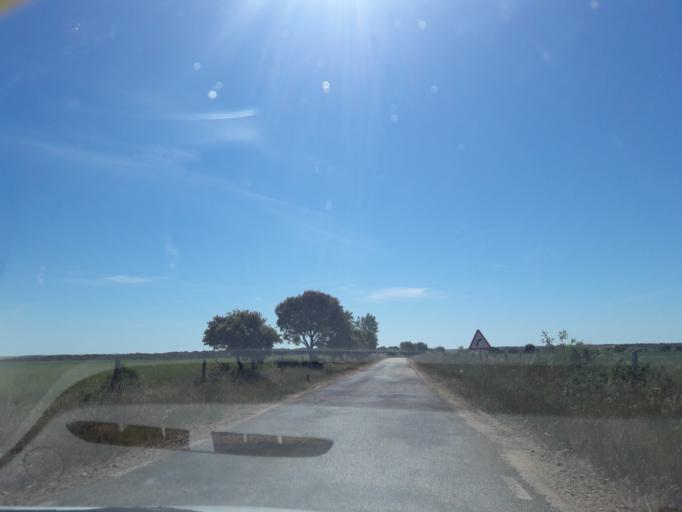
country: ES
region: Castille and Leon
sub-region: Provincia de Salamanca
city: Vega de Tirados
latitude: 41.0501
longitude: -5.8806
